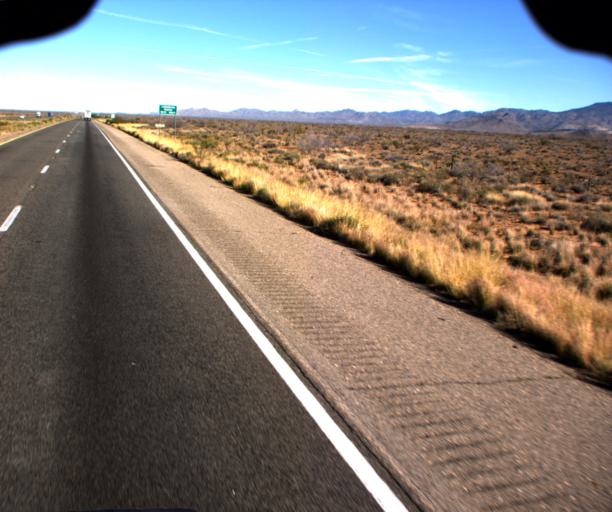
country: US
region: Arizona
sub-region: Mohave County
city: Golden Valley
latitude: 35.2881
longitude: -114.1804
